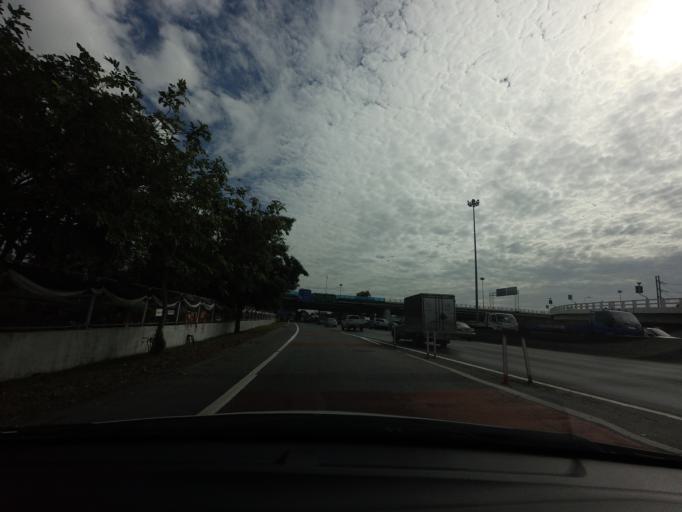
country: TH
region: Pathum Thani
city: Thanyaburi
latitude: 14.0073
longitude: 100.7037
